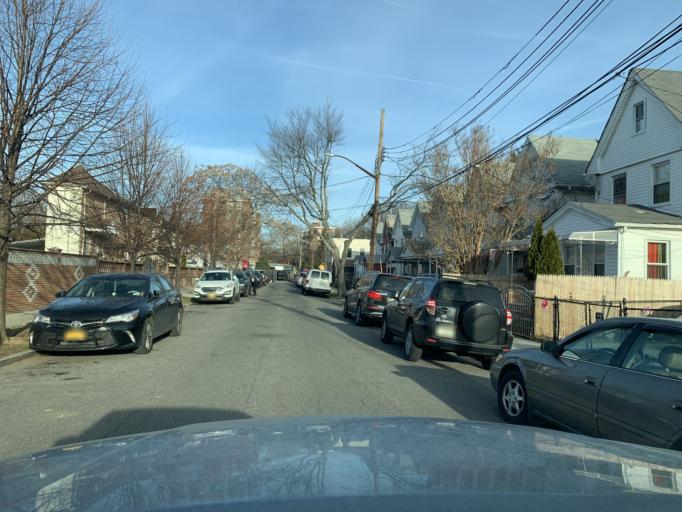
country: US
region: New York
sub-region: Queens County
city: Jamaica
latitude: 40.6913
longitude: -73.7911
